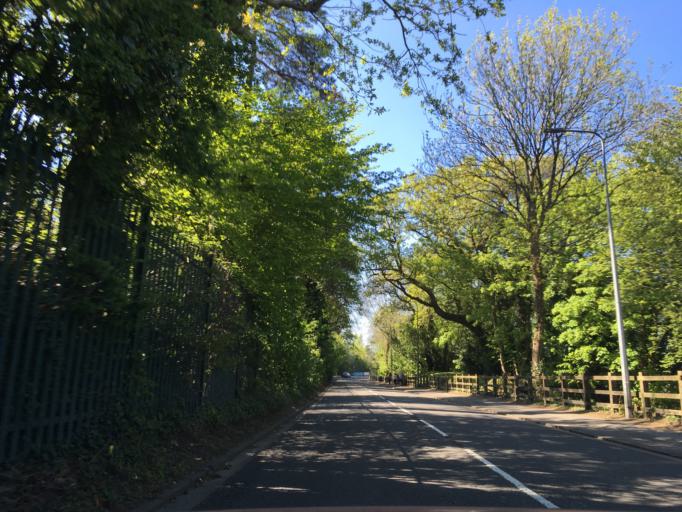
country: GB
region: Wales
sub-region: Cardiff
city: Radyr
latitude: 51.4984
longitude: -3.2258
